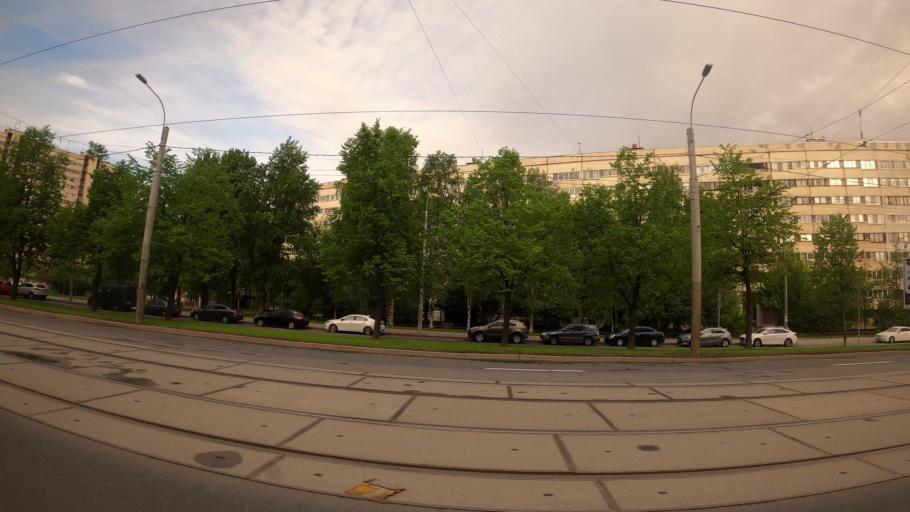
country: RU
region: St.-Petersburg
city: Vasyl'evsky Ostrov
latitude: 59.9450
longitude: 30.2302
